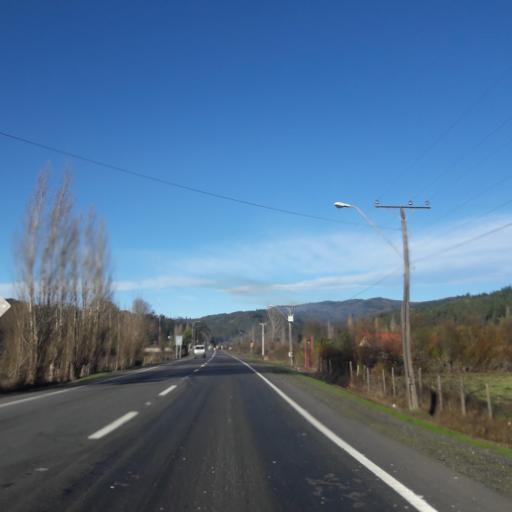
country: CL
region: Biobio
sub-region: Provincia de Concepcion
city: Lota
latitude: -37.2219
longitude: -72.9600
